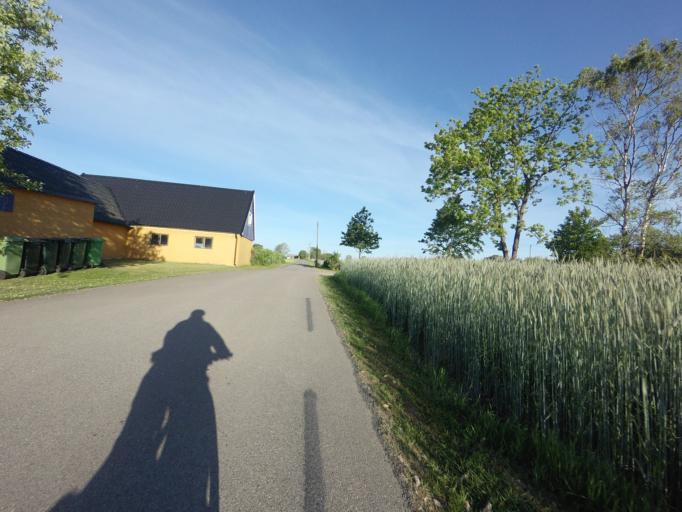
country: SE
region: Skane
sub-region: Hoganas Kommun
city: Hoganas
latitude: 56.2453
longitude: 12.6562
